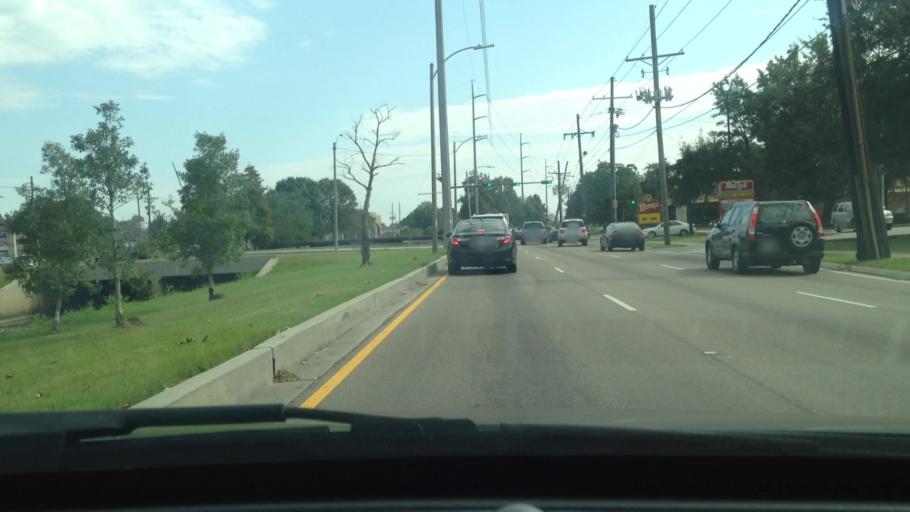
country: US
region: Louisiana
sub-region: Jefferson Parish
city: Terrytown
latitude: 29.9252
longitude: -90.0223
